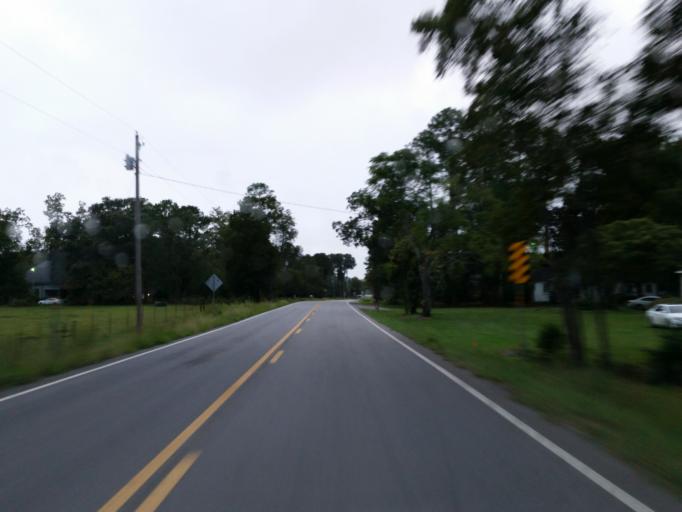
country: US
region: Georgia
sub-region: Crisp County
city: Cordele
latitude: 31.9013
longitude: -83.7615
